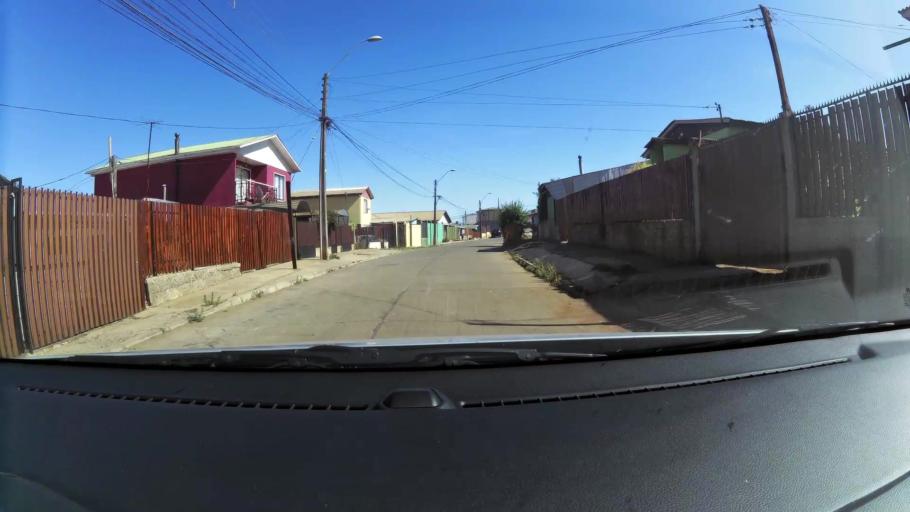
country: CL
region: Valparaiso
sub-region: Provincia de Valparaiso
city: Valparaiso
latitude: -33.0549
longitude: -71.6465
